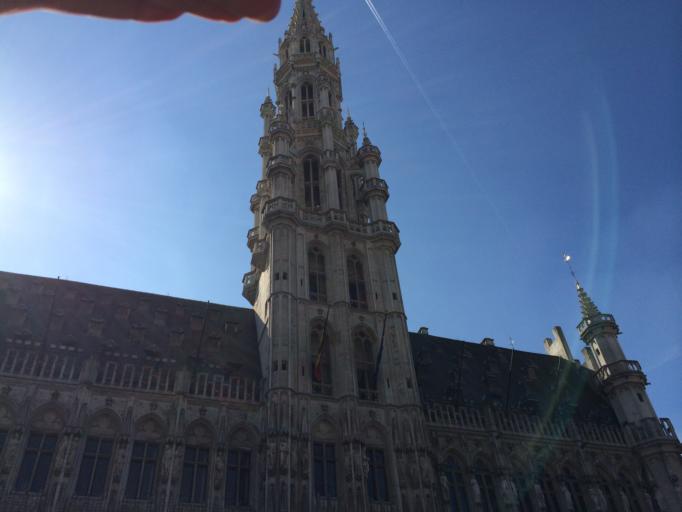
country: BE
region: Brussels Capital
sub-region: Bruxelles-Capitale
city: Brussels
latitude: 50.8467
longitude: 4.3524
